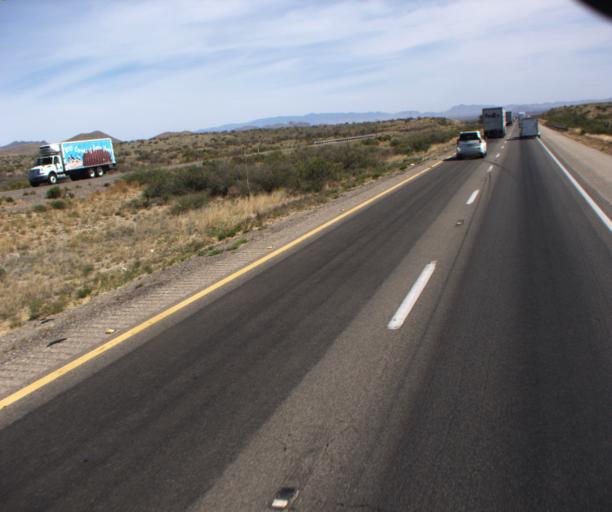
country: US
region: Arizona
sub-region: Cochise County
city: Willcox
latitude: 32.1301
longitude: -110.0090
